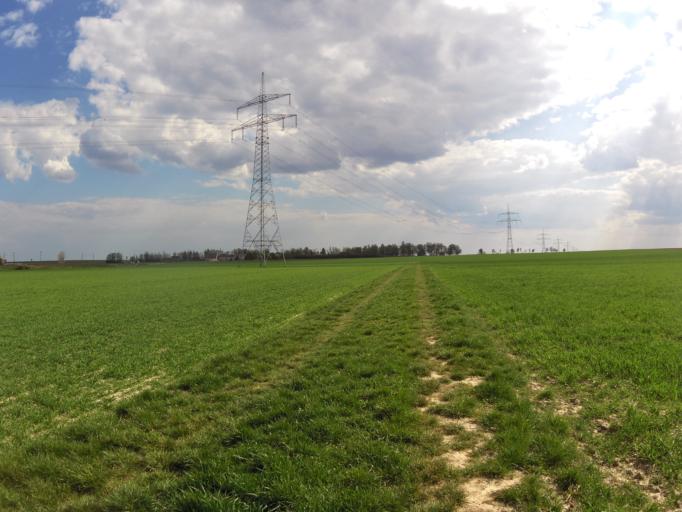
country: DE
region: Bavaria
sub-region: Regierungsbezirk Unterfranken
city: Oberpleichfeld
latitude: 49.8613
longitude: 10.0977
